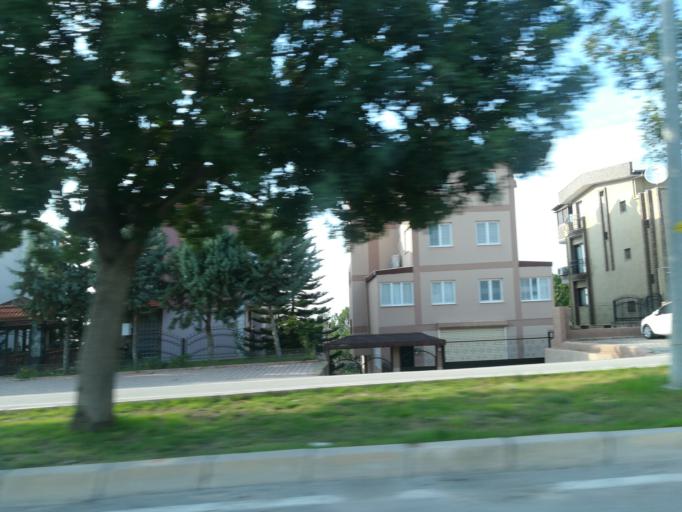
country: TR
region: Adana
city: Adana
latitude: 37.0758
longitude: 35.3873
